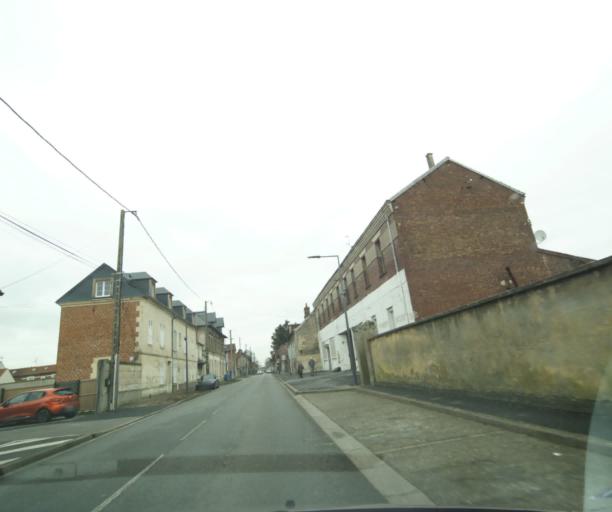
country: FR
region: Picardie
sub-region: Departement de l'Oise
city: Noyon
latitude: 49.5735
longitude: 3.0140
